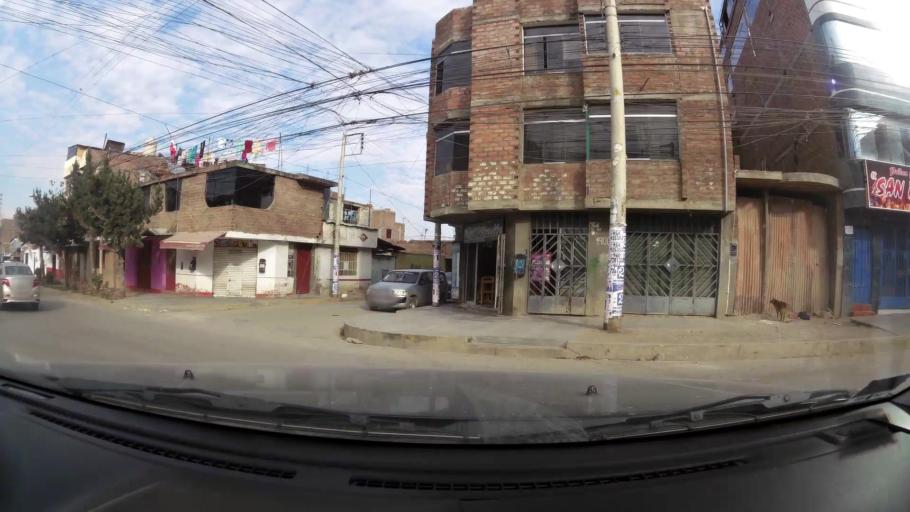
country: PE
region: Junin
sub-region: Provincia de Huancayo
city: Huancayo
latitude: -12.0426
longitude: -75.1935
